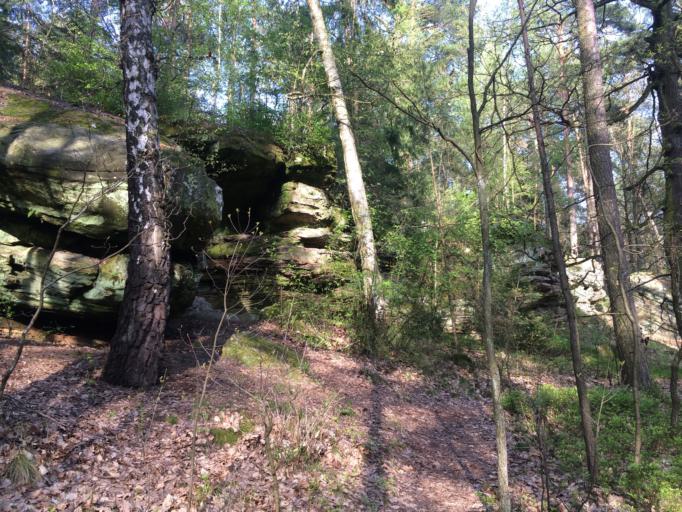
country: PL
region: Swietokrzyskie
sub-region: Powiat starachowicki
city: Brody
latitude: 51.0323
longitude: 21.1650
